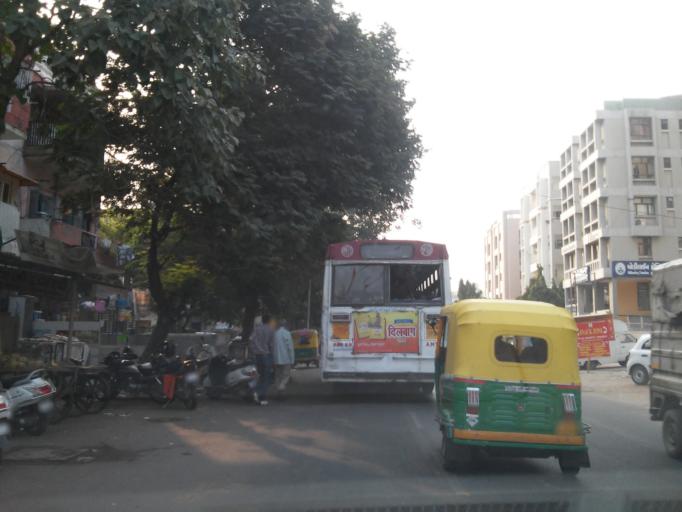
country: IN
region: Gujarat
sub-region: Ahmadabad
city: Ahmedabad
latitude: 23.0099
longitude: 72.5550
